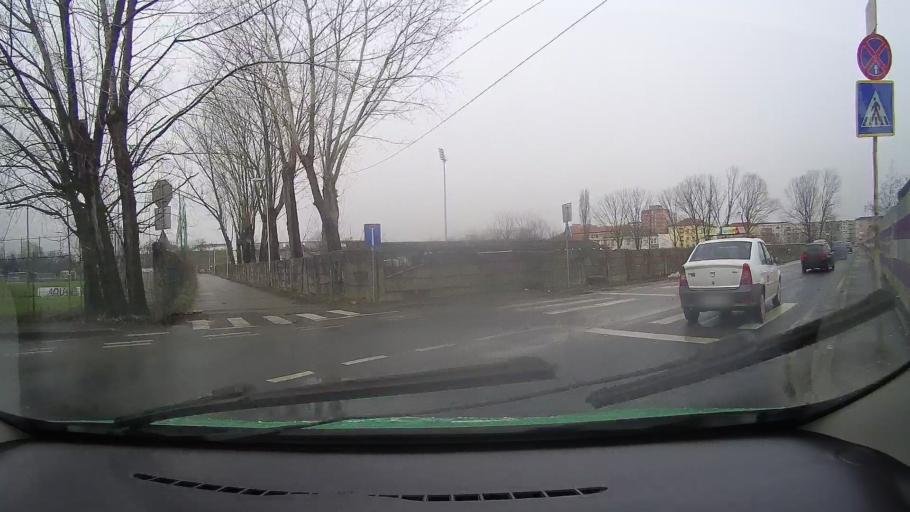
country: RO
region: Timis
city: Timisoara
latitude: 45.7408
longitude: 21.2485
